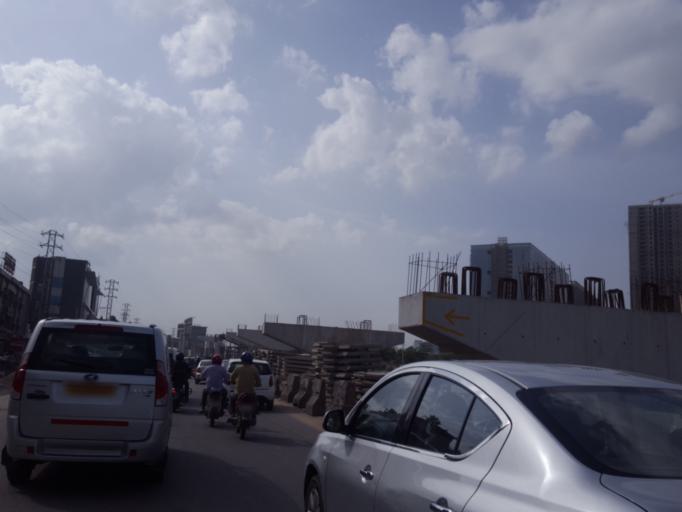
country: IN
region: Telangana
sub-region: Rangareddi
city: Kukatpalli
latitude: 17.4258
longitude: 78.3778
